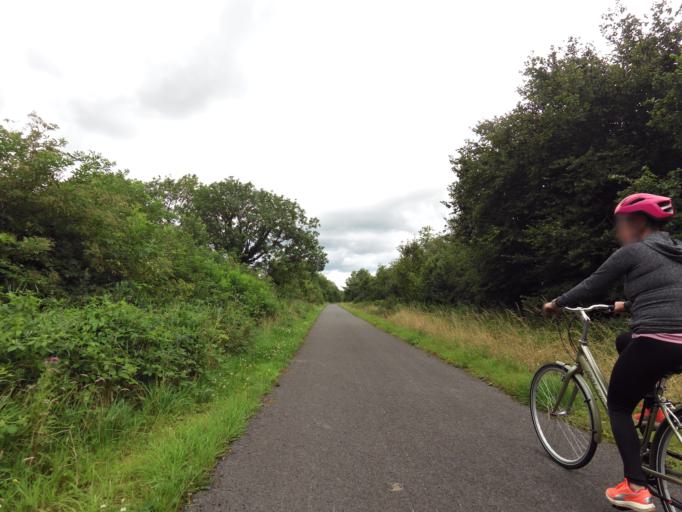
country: IE
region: Leinster
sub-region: An Iarmhi
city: An Muileann gCearr
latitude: 53.5033
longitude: -7.4302
